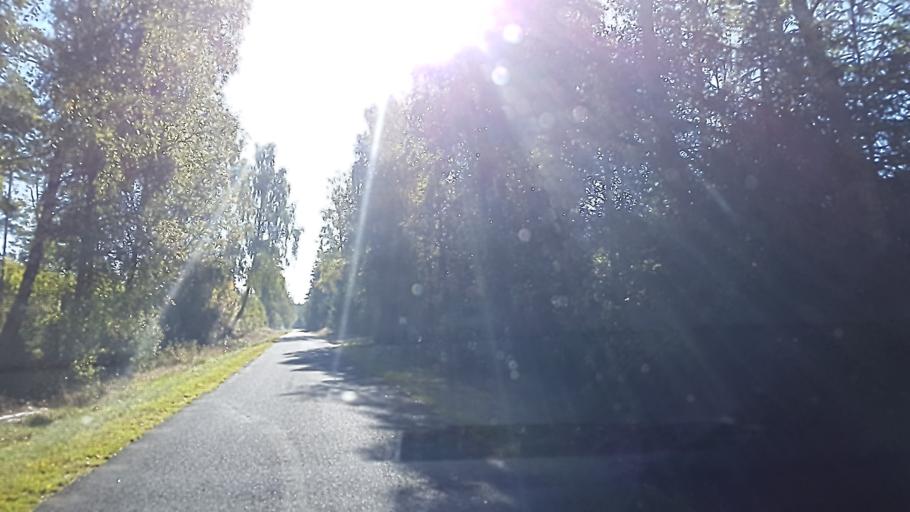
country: SE
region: Kronoberg
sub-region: Ljungby Kommun
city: Ljungby
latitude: 56.8067
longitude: 14.0262
